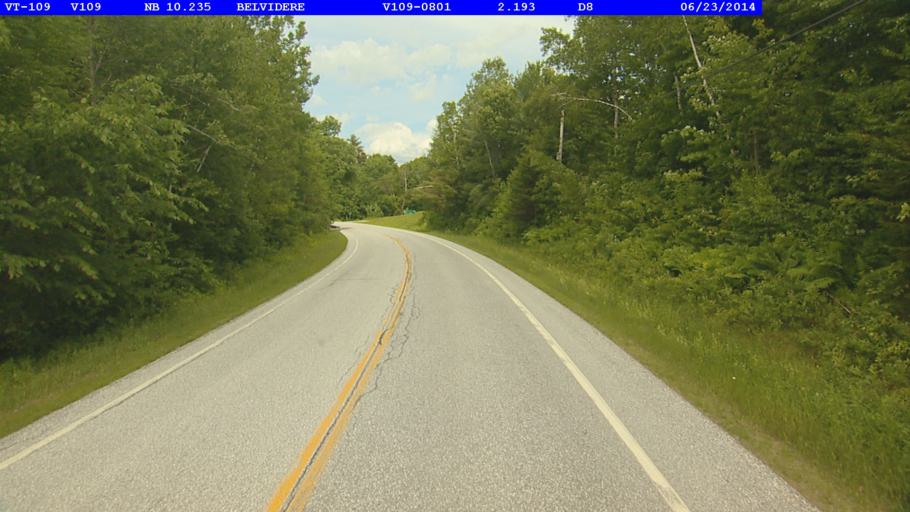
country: US
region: Vermont
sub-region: Lamoille County
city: Johnson
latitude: 44.7470
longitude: -72.7032
